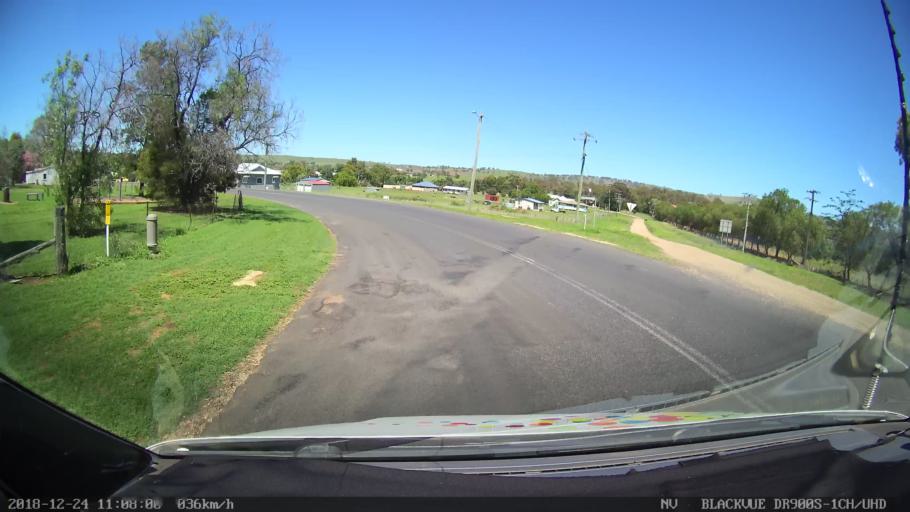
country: AU
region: New South Wales
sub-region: Upper Hunter Shire
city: Merriwa
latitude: -32.1355
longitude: 150.3573
